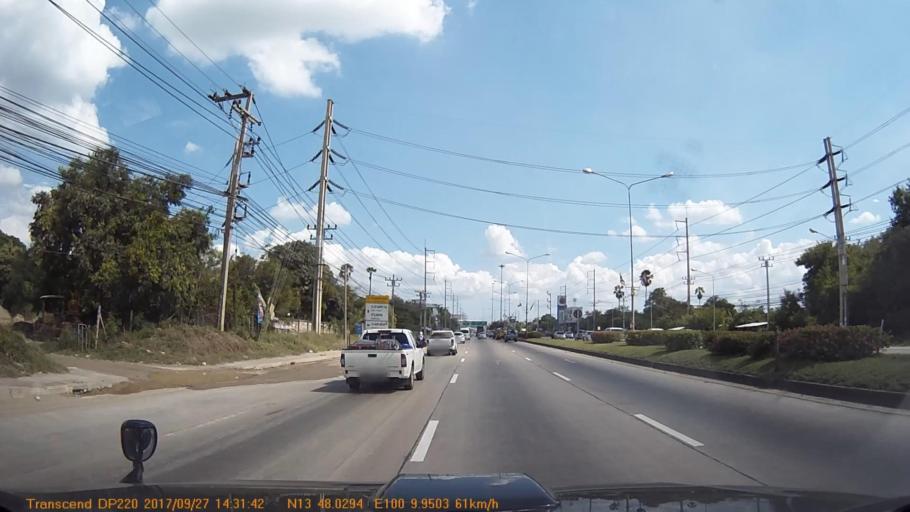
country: TH
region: Nakhon Pathom
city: Nakhon Chai Si
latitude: 13.8005
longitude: 100.1658
